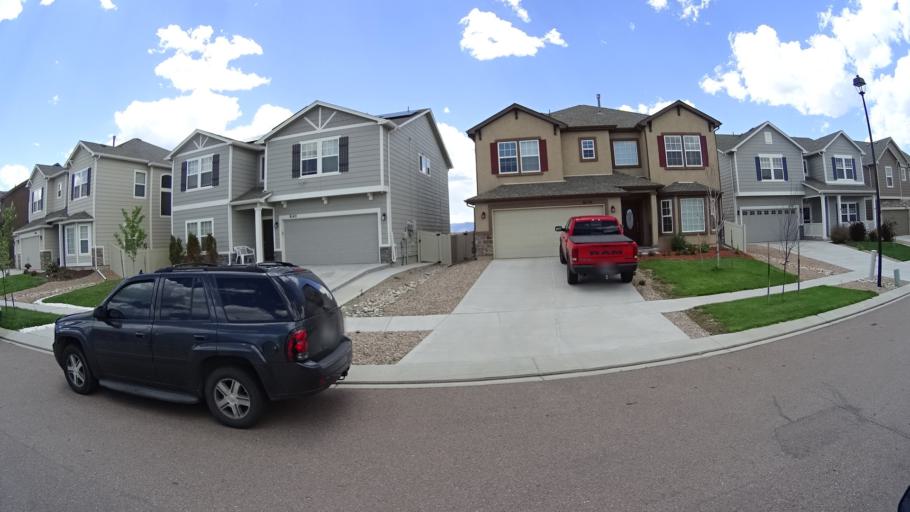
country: US
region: Colorado
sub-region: El Paso County
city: Black Forest
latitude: 38.9505
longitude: -104.7048
